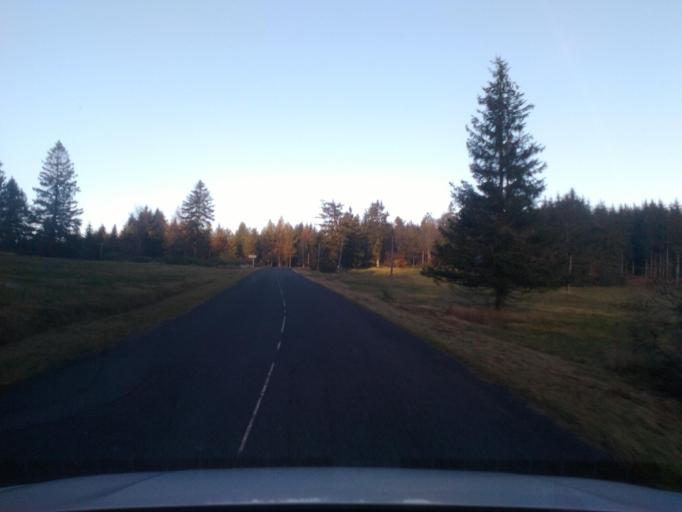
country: FR
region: Lorraine
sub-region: Departement des Vosges
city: Senones
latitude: 48.3737
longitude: 7.0979
